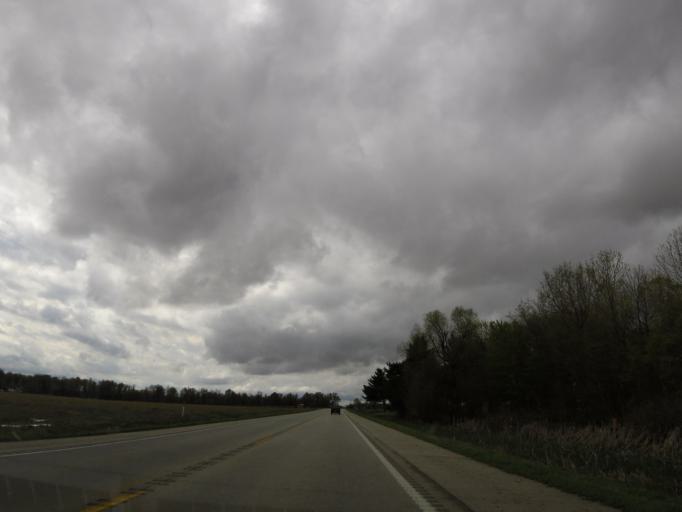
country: US
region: Arkansas
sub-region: Clay County
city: Corning
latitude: 36.5963
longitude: -90.5206
